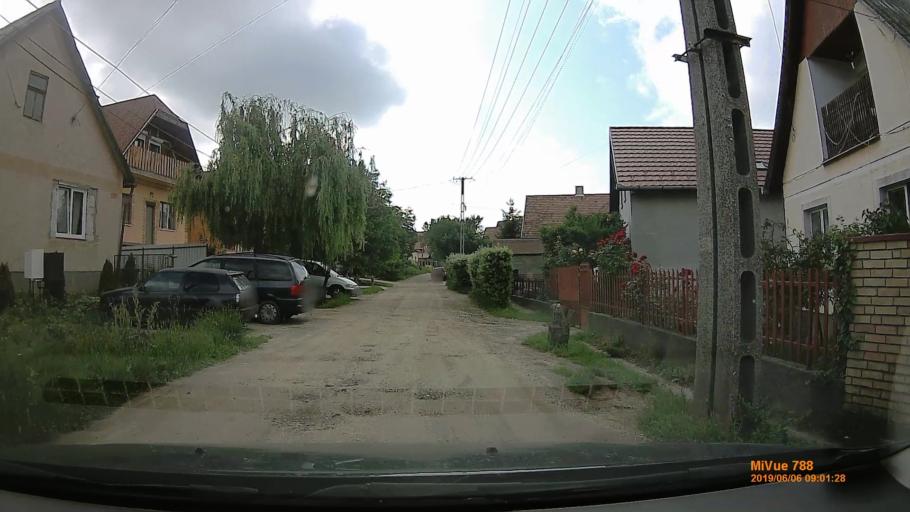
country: HU
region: Pest
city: Maglod
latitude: 47.4501
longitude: 19.3449
